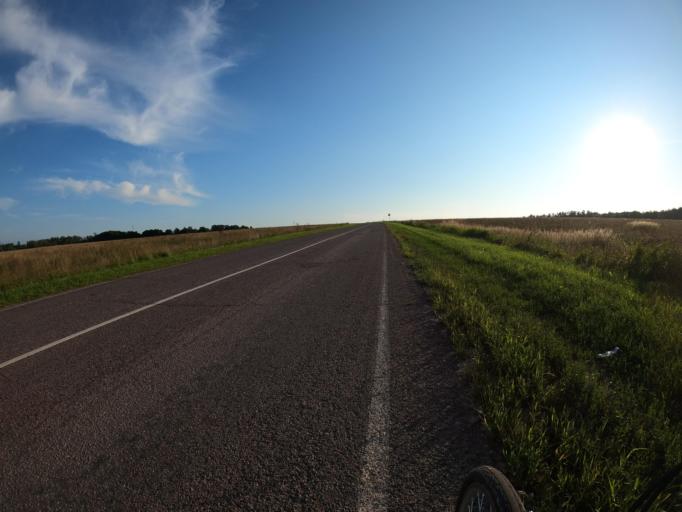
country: RU
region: Moskovskaya
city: Meshcherino
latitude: 55.1232
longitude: 38.3293
